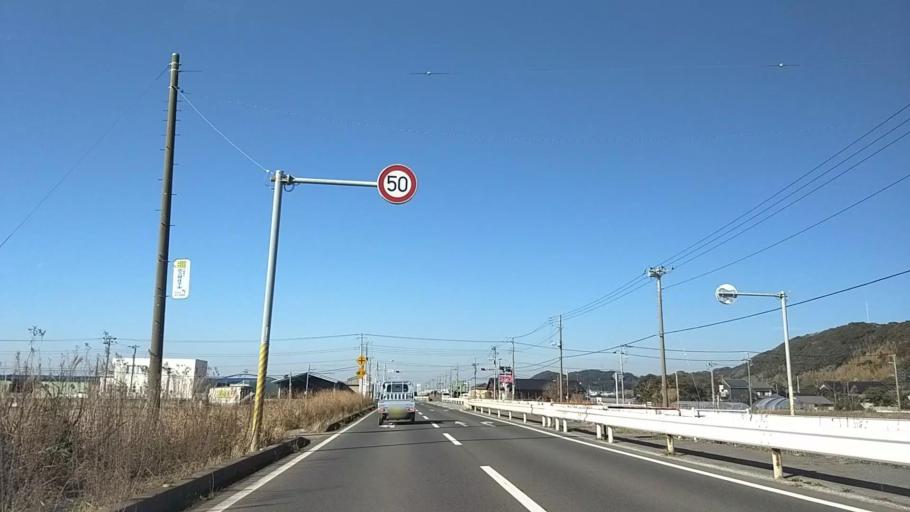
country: JP
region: Chiba
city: Asahi
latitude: 35.7098
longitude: 140.7188
